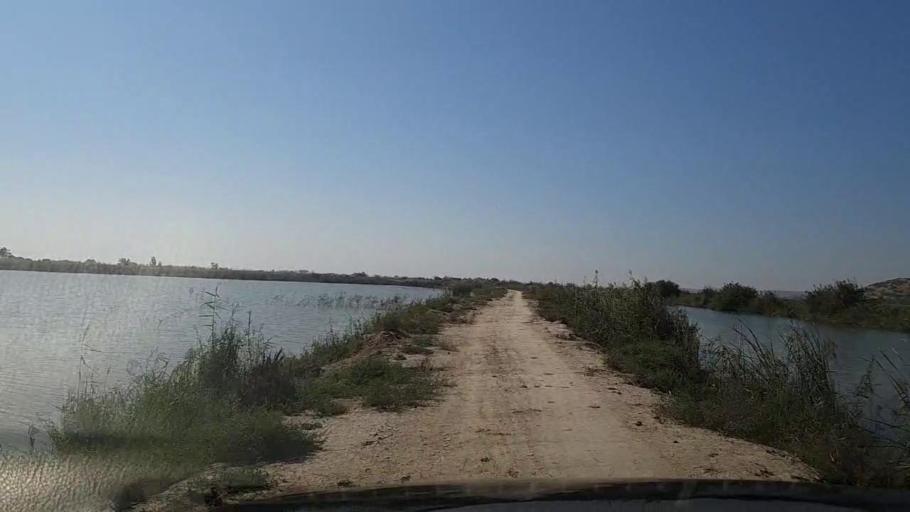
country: PK
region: Sindh
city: Thatta
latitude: 24.6758
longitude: 67.8892
